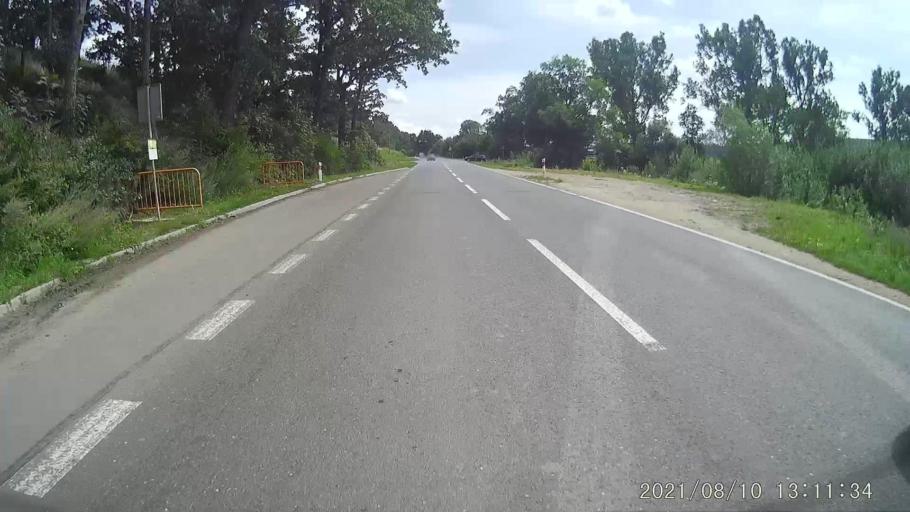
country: PL
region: Lower Silesian Voivodeship
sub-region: Powiat klodzki
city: Bozkow
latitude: 50.5088
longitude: 16.5179
